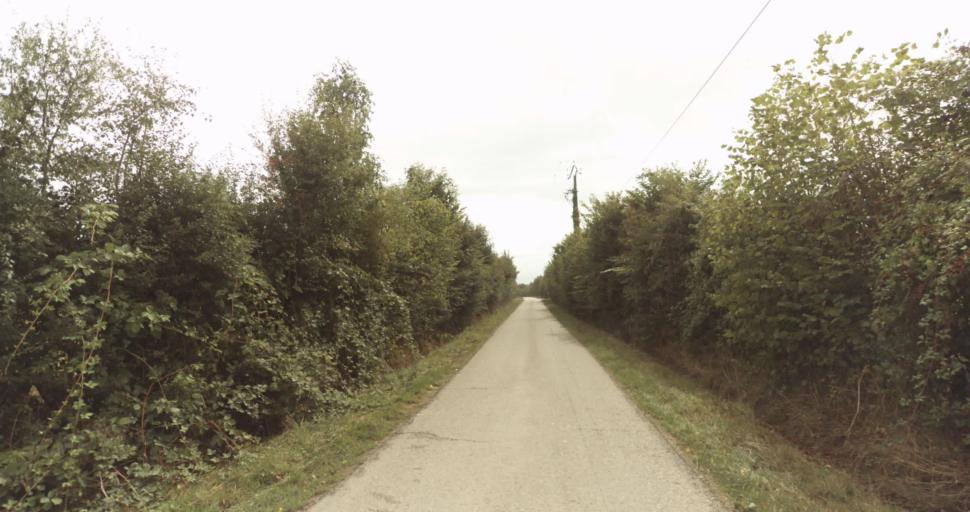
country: FR
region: Lower Normandy
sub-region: Departement de l'Orne
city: Gace
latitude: 48.8224
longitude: 0.3127
